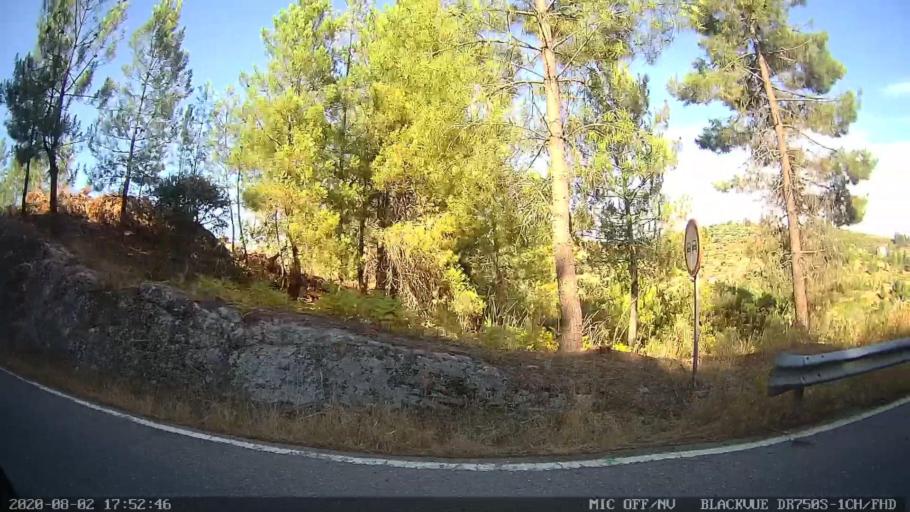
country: PT
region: Vila Real
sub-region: Murca
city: Murca
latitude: 41.4066
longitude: -7.4689
